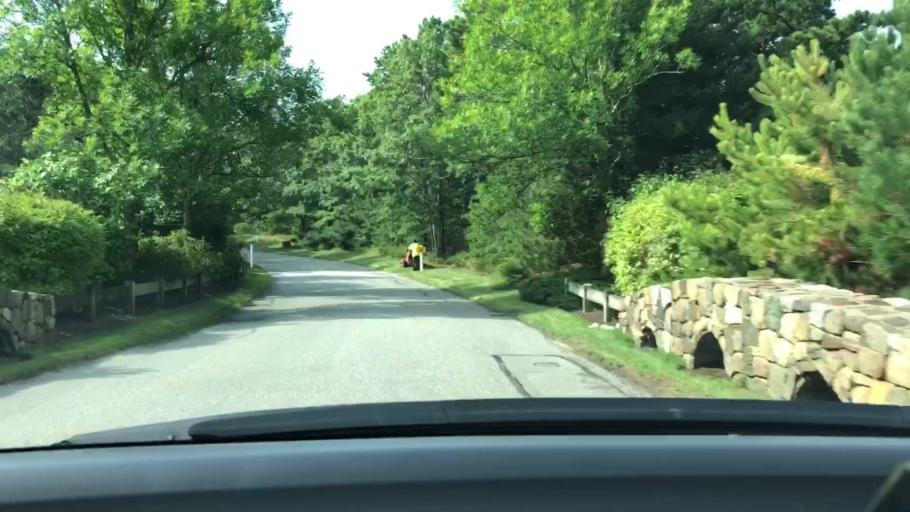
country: US
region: Massachusetts
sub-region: Plymouth County
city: Plymouth
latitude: 41.8898
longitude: -70.6002
